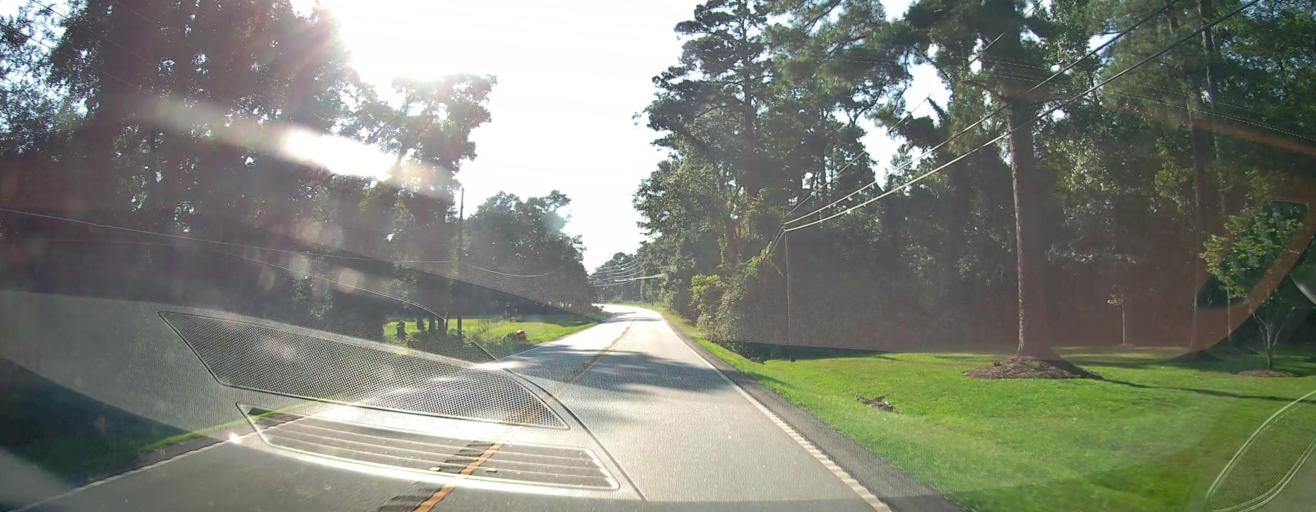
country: US
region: Georgia
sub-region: Houston County
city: Robins Air Force Base
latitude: 32.5022
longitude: -83.6241
